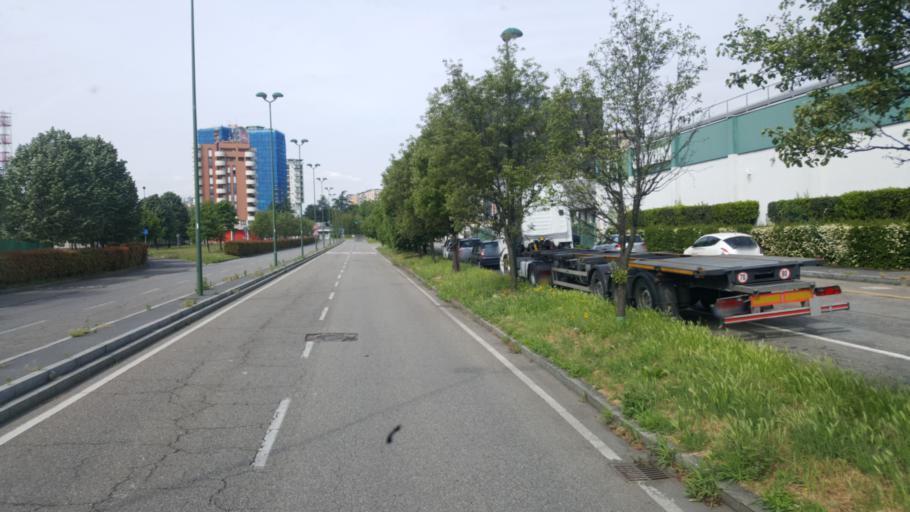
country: IT
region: Lombardy
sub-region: Citta metropolitana di Milano
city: Sesto San Giovanni
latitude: 45.5495
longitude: 9.2407
